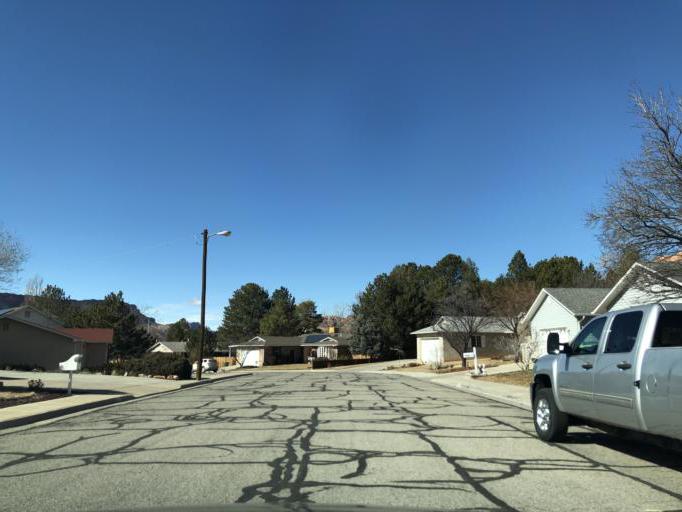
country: US
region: Utah
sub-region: Grand County
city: Moab
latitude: 38.5846
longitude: -109.5571
